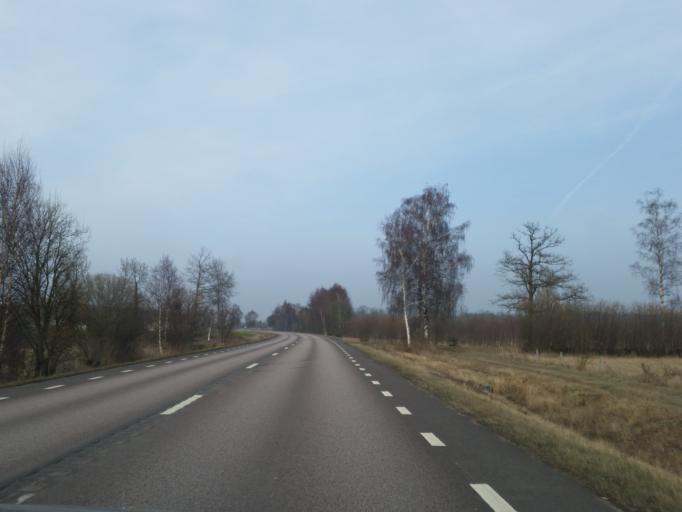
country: SE
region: Kalmar
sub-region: Borgholms Kommun
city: Borgholm
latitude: 57.1085
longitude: 16.9465
